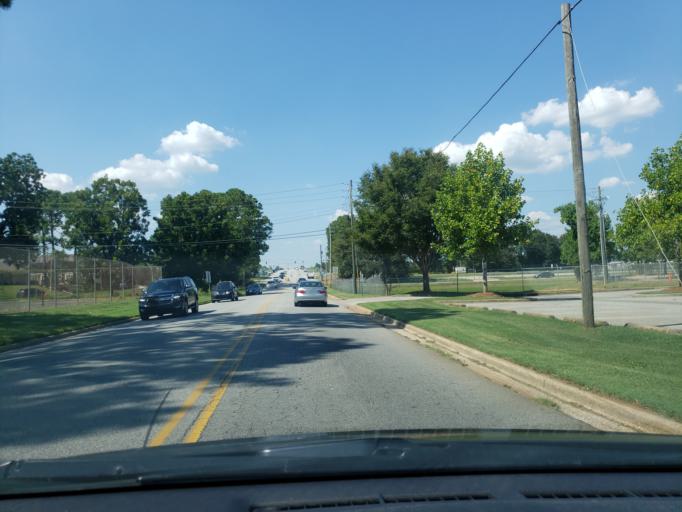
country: US
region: Georgia
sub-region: Dougherty County
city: Albany
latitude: 31.6128
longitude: -84.2042
